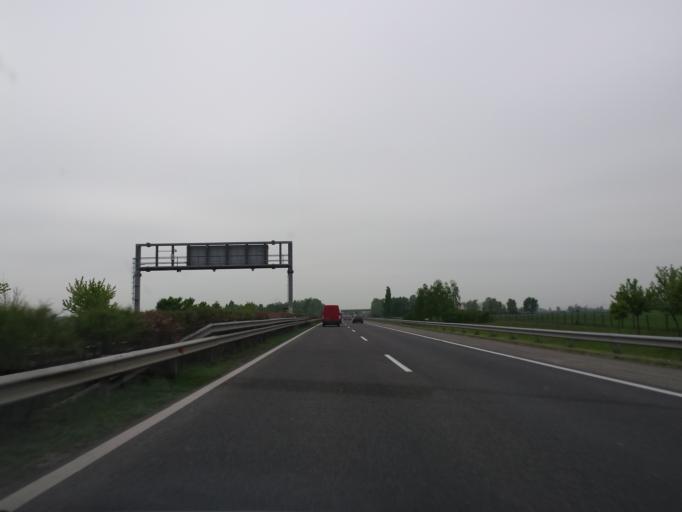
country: HU
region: Gyor-Moson-Sopron
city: Abda
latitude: 47.6915
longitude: 17.5245
